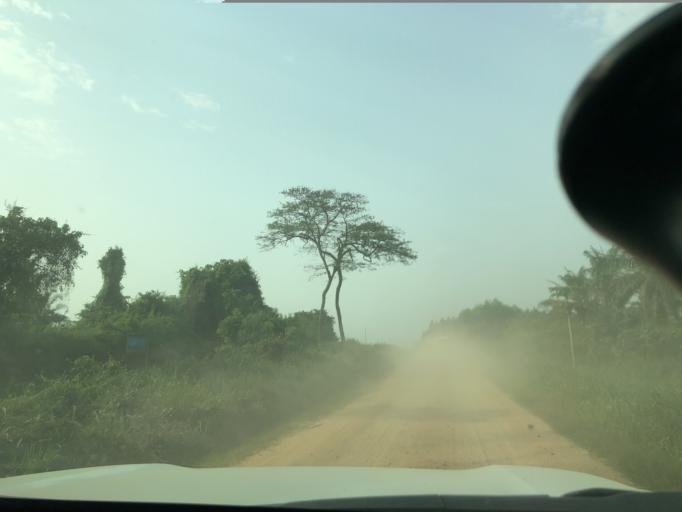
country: UG
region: Western Region
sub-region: Kasese District
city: Margherita
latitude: 0.1864
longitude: 29.6586
